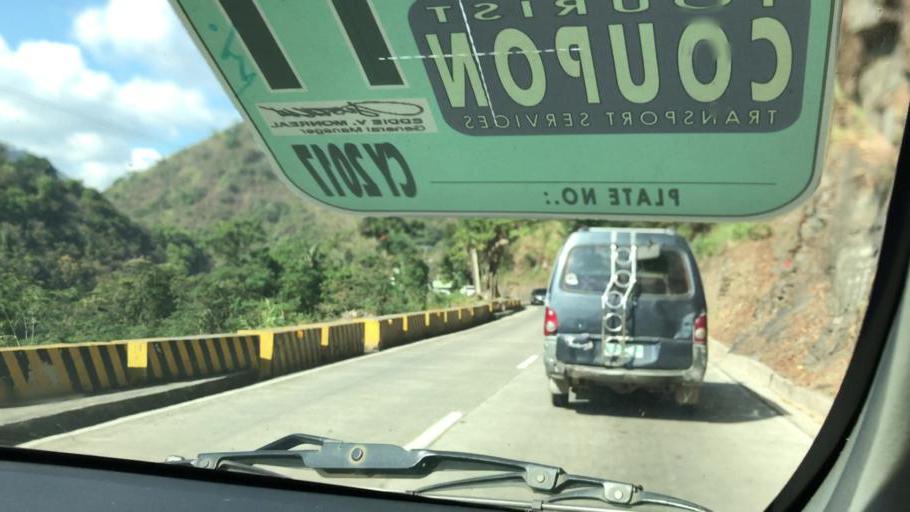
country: PH
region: Cordillera
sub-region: Province of Benguet
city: Tuba
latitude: 16.3128
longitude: 120.6174
